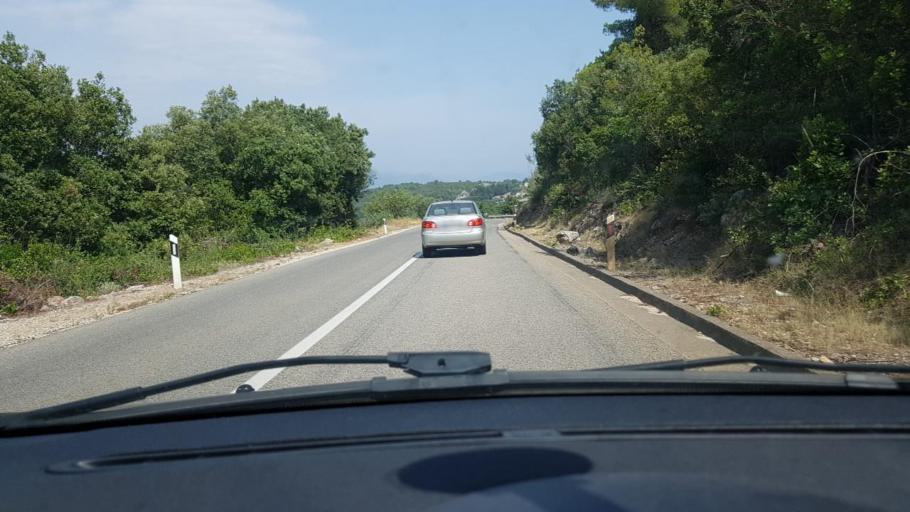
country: HR
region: Dubrovacko-Neretvanska
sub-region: Grad Korcula
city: Zrnovo
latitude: 42.9378
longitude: 17.0951
